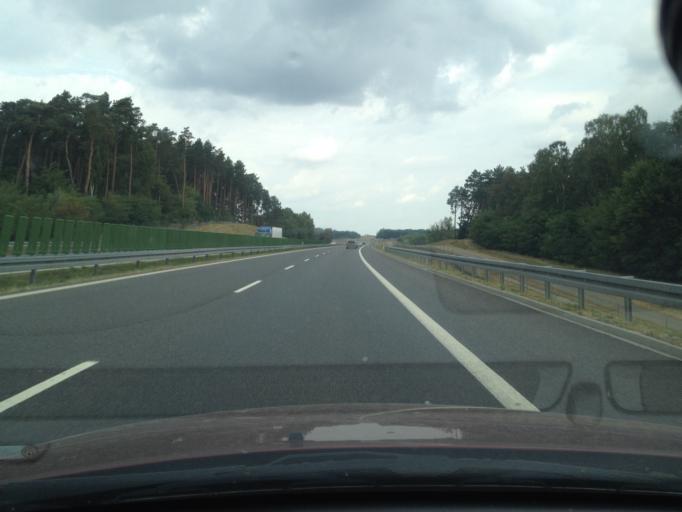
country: PL
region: West Pomeranian Voivodeship
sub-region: Powiat mysliborski
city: Mysliborz
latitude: 52.9974
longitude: 14.8624
